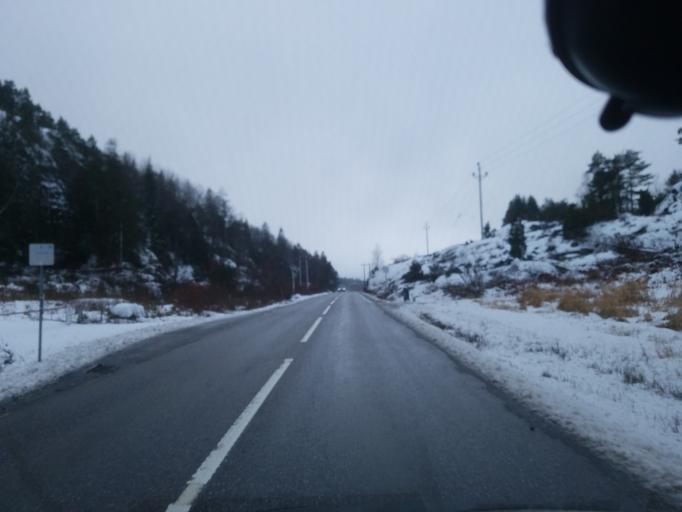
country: SE
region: Vaestra Goetaland
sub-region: Orust
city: Henan
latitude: 58.3146
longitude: 11.6226
